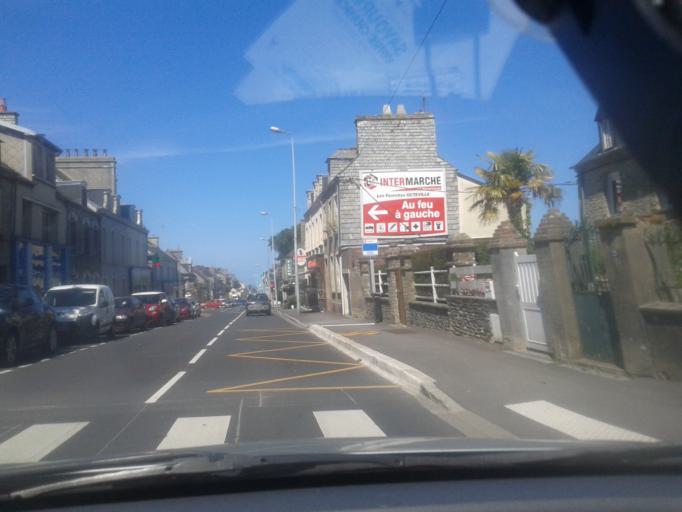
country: FR
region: Lower Normandy
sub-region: Departement de la Manche
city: Octeville
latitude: 49.6284
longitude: -1.6417
